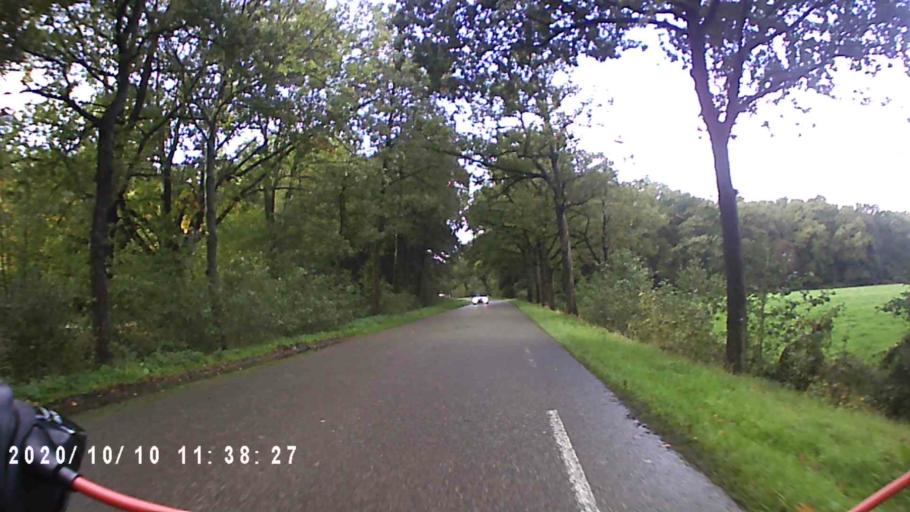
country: NL
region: Friesland
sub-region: Gemeente Smallingerland
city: Drachten
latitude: 53.0713
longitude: 6.1101
